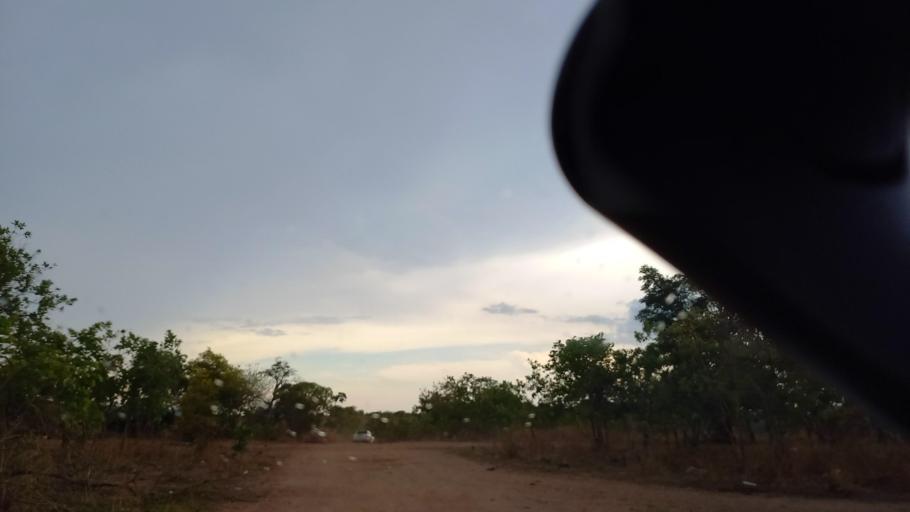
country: ZM
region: Lusaka
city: Kafue
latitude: -15.9876
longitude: 28.2672
